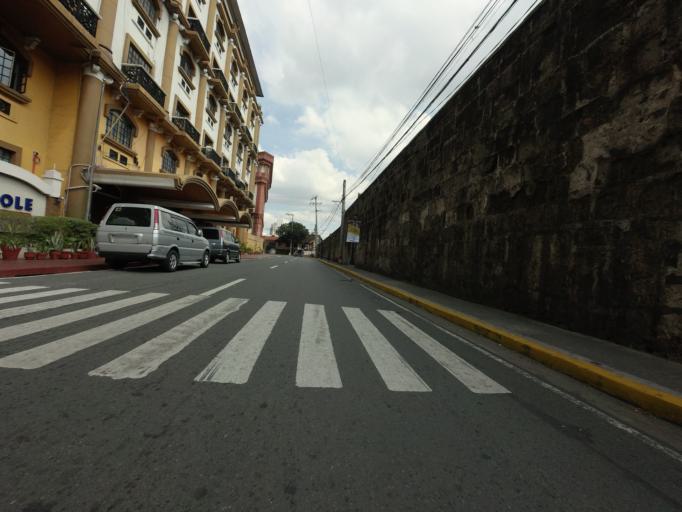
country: PH
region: Metro Manila
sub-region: City of Manila
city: Port Area
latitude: 14.5866
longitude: 120.9778
